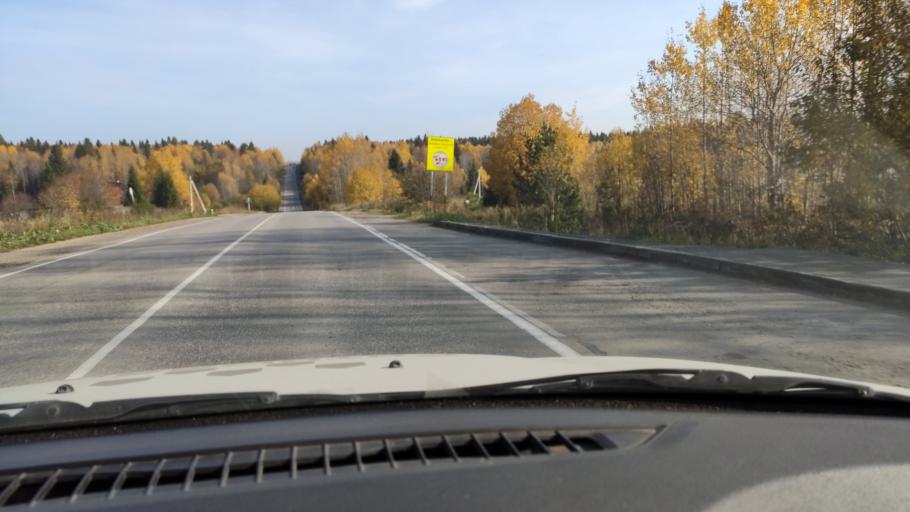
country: RU
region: Perm
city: Novyye Lyady
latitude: 58.0263
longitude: 56.6760
